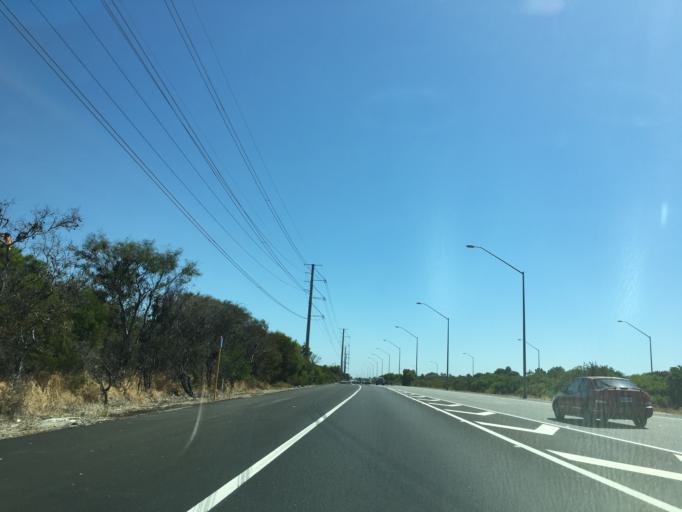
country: AU
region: Western Australia
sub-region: Canning
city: Canning Vale
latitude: -32.0592
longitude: 115.9026
